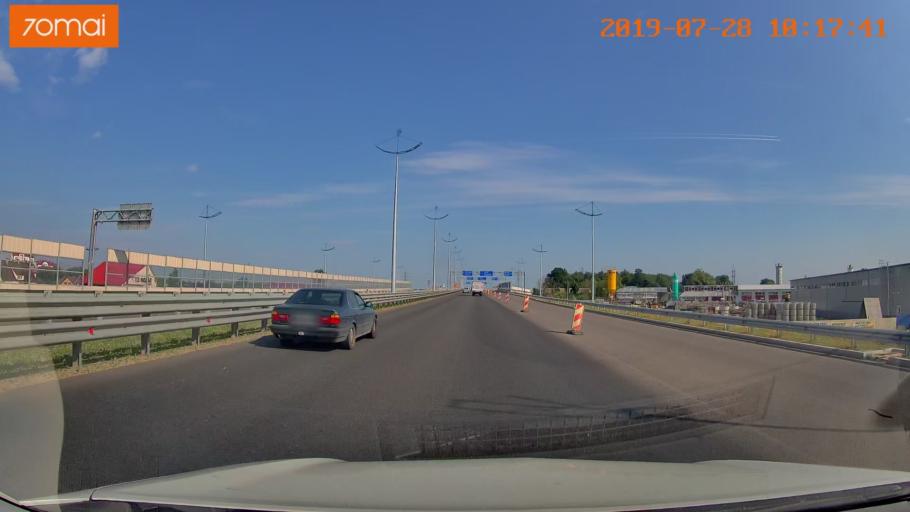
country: RU
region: Kaliningrad
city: Maloye Isakovo
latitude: 54.7430
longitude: 20.5930
